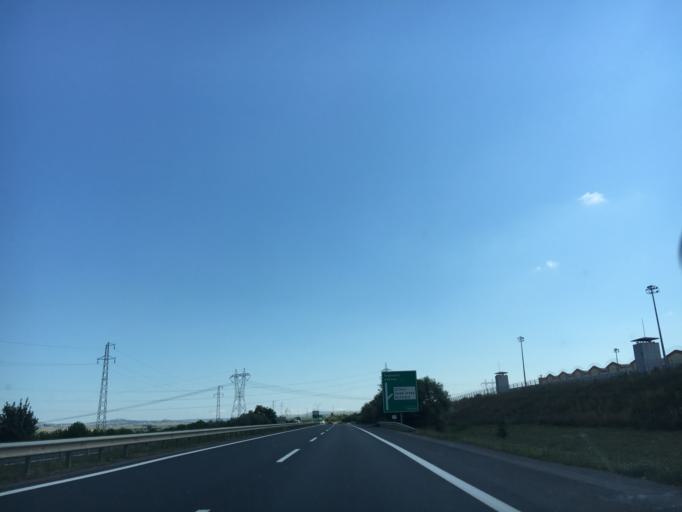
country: TR
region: Istanbul
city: Canta
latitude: 41.0890
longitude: 28.1412
